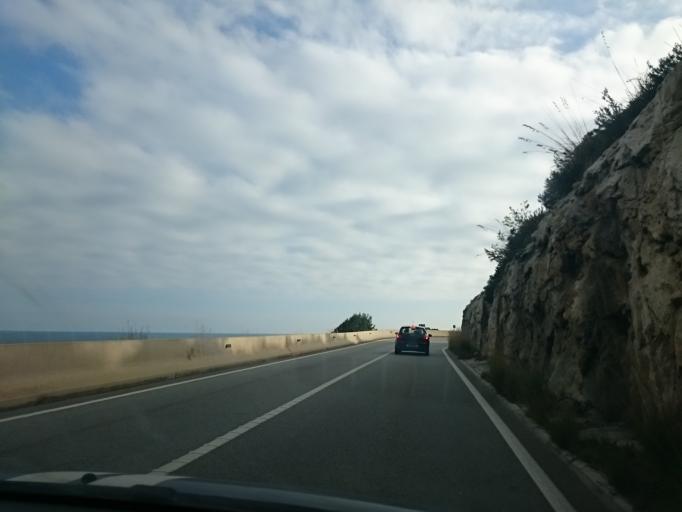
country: ES
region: Catalonia
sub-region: Provincia de Barcelona
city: Sitges
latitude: 41.2421
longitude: 1.8675
